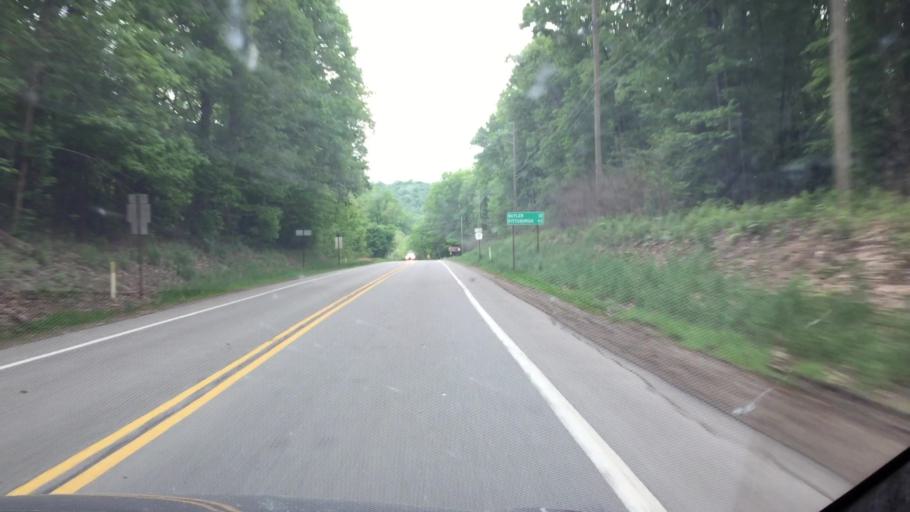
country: US
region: Pennsylvania
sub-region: Butler County
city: Slippery Rock
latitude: 41.0096
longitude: -80.0016
